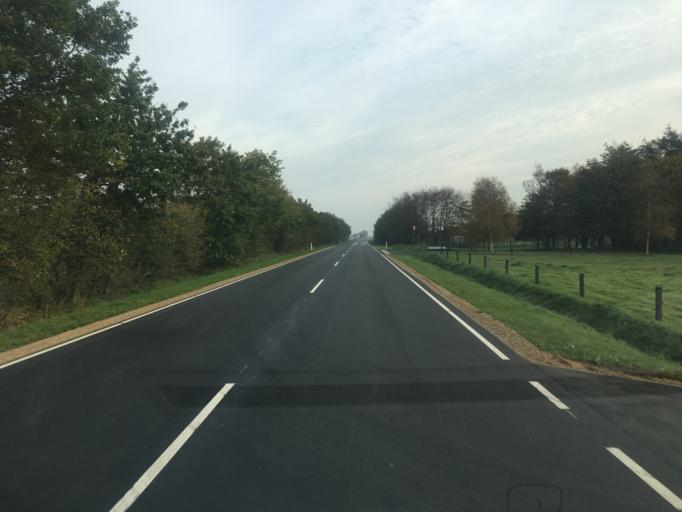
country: DK
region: South Denmark
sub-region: Tonder Kommune
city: Logumkloster
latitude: 55.0715
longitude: 8.9703
